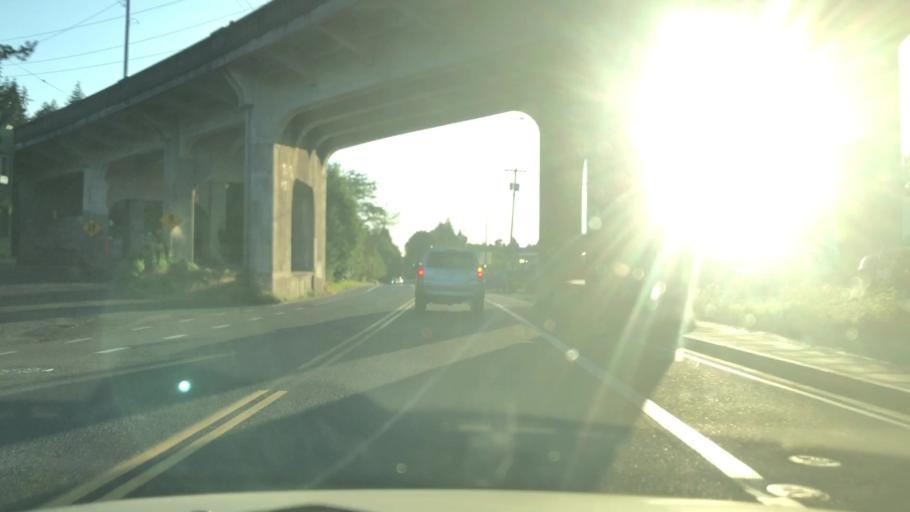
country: US
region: Oregon
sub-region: Washington County
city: Garden Home-Whitford
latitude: 45.4719
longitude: -122.7198
